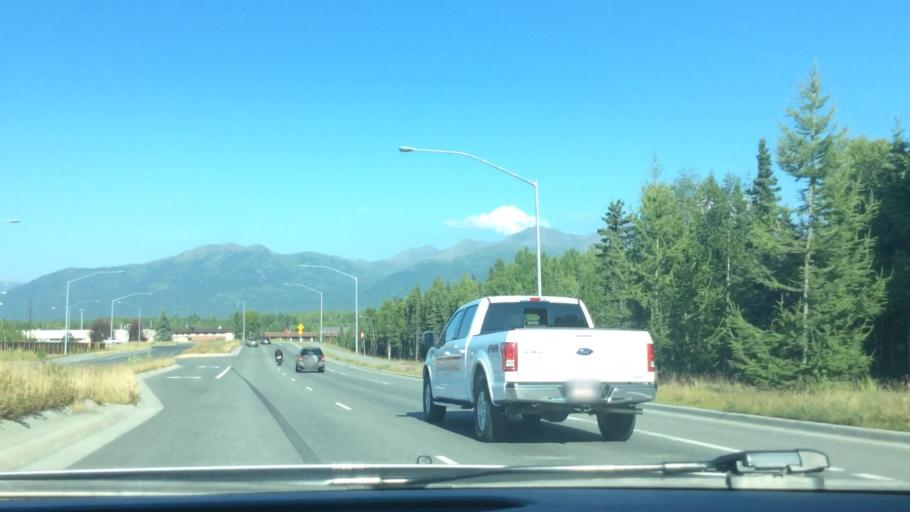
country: US
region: Alaska
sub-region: Anchorage Municipality
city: Anchorage
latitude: 61.1784
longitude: -149.7841
